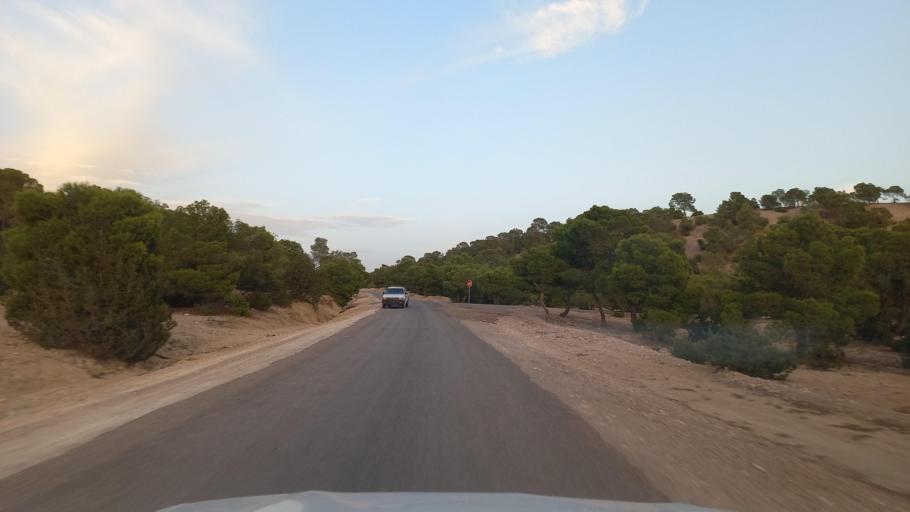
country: TN
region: Al Qasrayn
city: Sbiba
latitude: 35.4106
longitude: 8.9617
